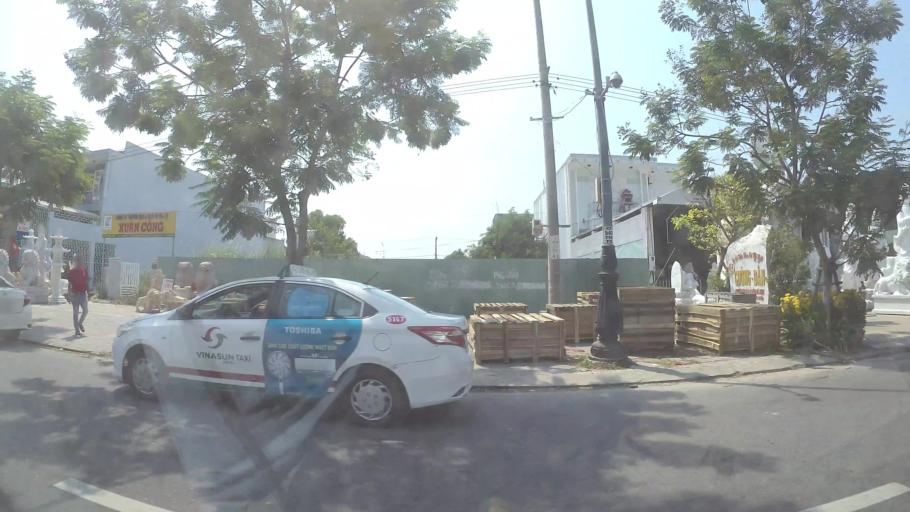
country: VN
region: Da Nang
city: Ngu Hanh Son
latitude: 15.9983
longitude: 108.2675
